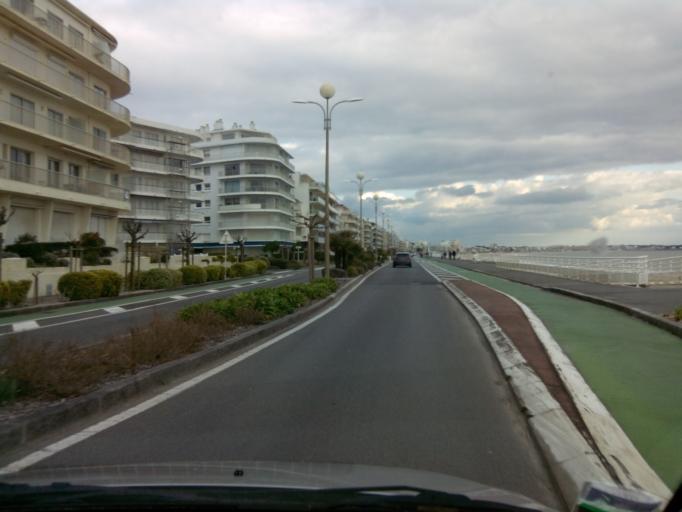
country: FR
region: Pays de la Loire
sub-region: Departement de la Loire-Atlantique
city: La Baule-Escoublac
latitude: 47.2796
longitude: -2.3778
